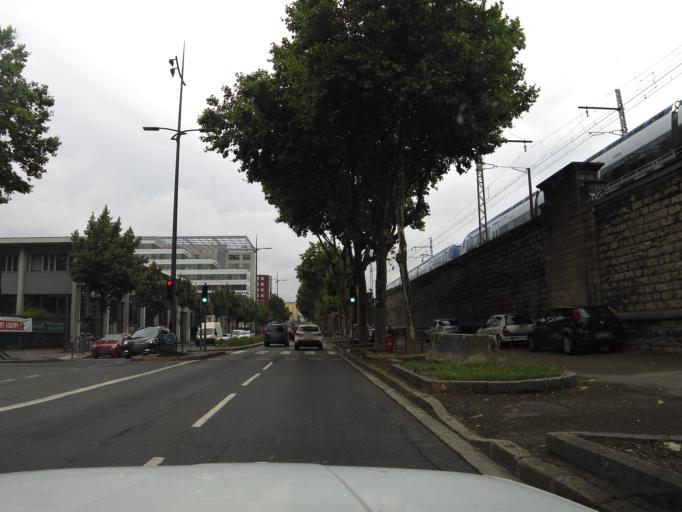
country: FR
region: Rhone-Alpes
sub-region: Departement du Rhone
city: Caluire-et-Cuire
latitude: 45.7748
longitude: 4.8590
